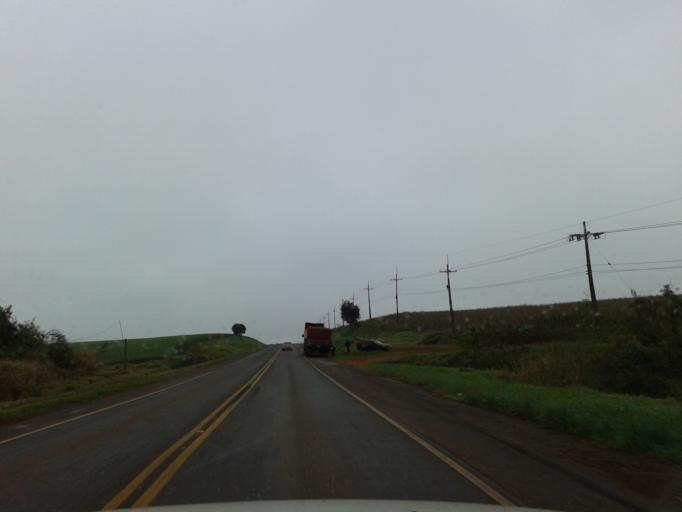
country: PY
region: Alto Parana
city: Naranjal
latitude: -25.9053
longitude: -55.1186
